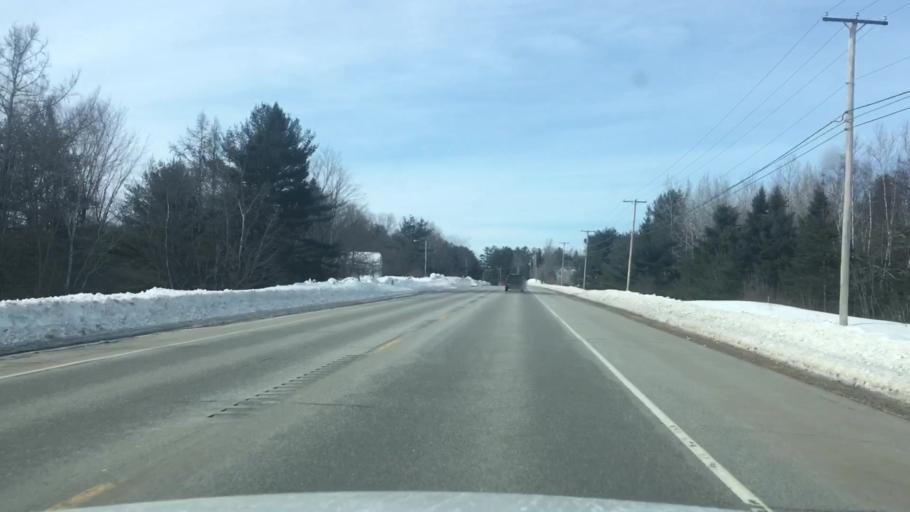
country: US
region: Maine
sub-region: Penobscot County
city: Kenduskeag
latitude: 44.9558
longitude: -68.9516
